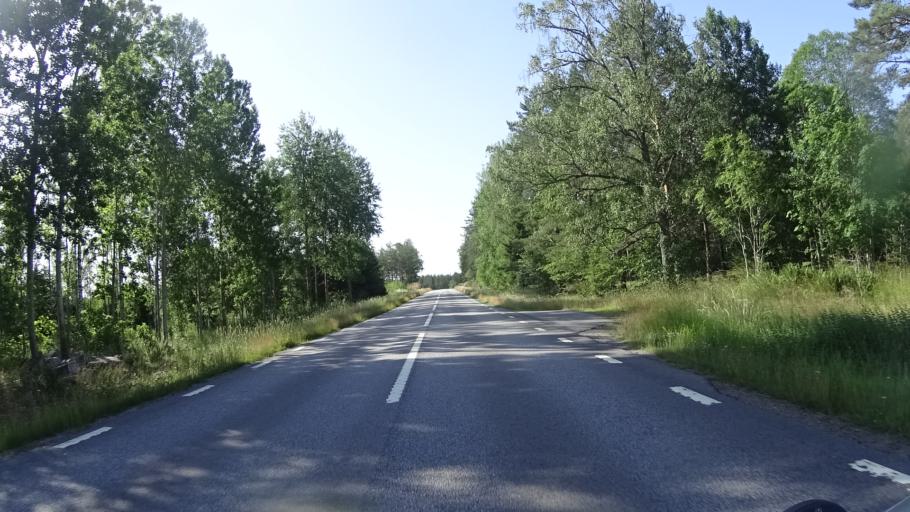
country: SE
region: OEstergoetland
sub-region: Atvidabergs Kommun
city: Atvidaberg
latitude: 58.1360
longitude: 16.0910
